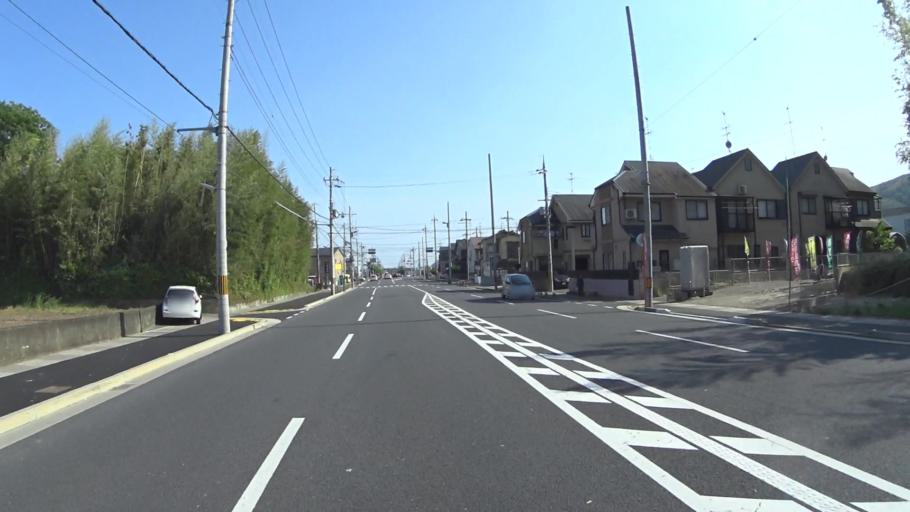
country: JP
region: Kyoto
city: Muko
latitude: 34.9414
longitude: 135.6858
